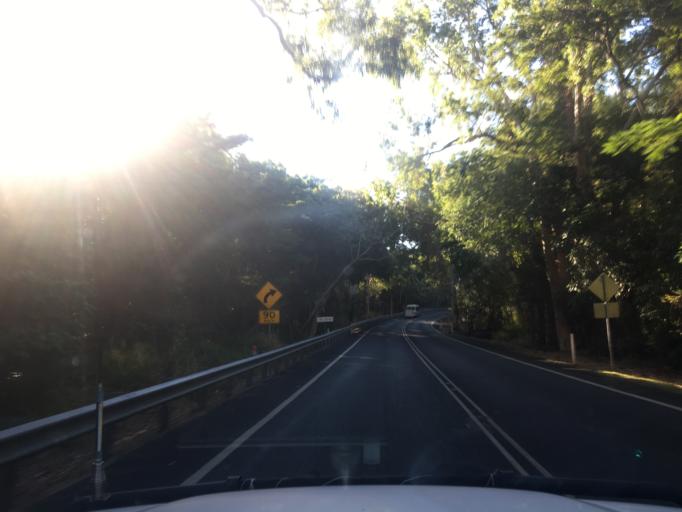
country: AU
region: Queensland
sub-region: Cairns
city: Palm Cove
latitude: -16.6659
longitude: 145.5672
